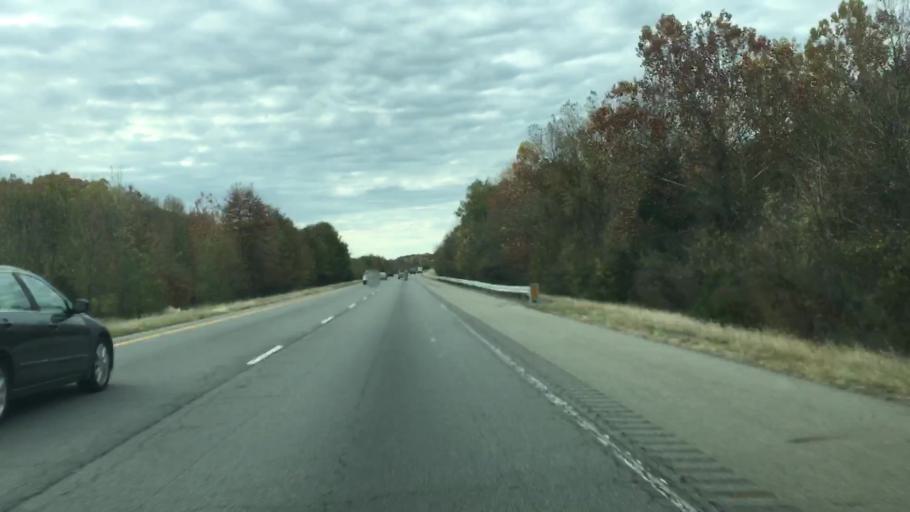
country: US
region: Arkansas
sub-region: Faulkner County
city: Conway
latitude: 35.1206
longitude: -92.4822
